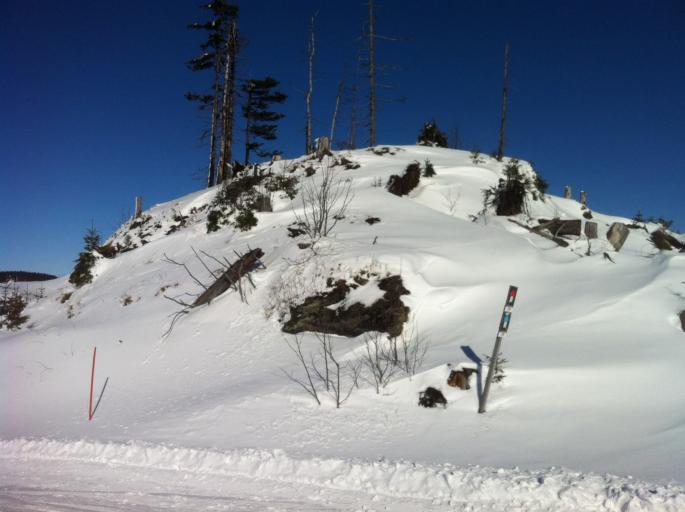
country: DE
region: Bavaria
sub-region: Lower Bavaria
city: Bodenmais
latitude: 49.0895
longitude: 13.1328
